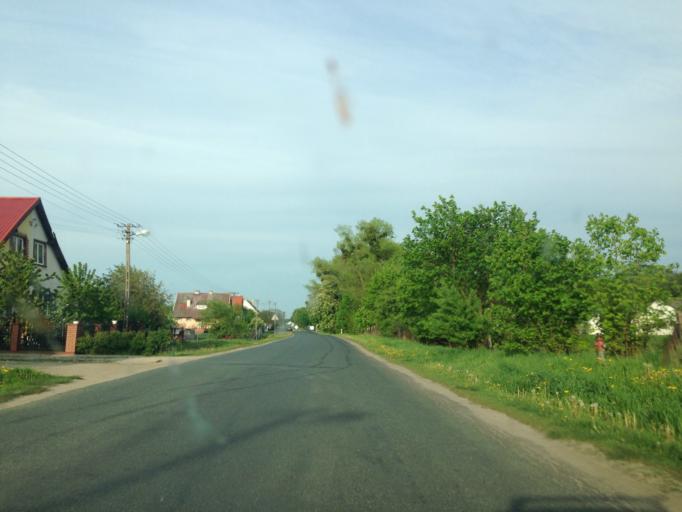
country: PL
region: Kujawsko-Pomorskie
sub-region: Powiat wabrzeski
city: Debowa Laka
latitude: 53.2514
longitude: 19.0333
